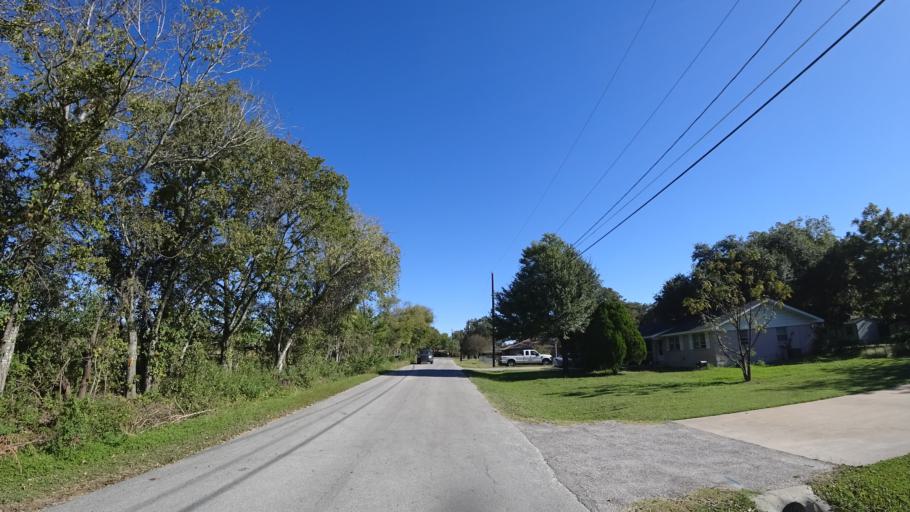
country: US
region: Texas
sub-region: Travis County
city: Manor
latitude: 30.3360
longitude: -97.6546
